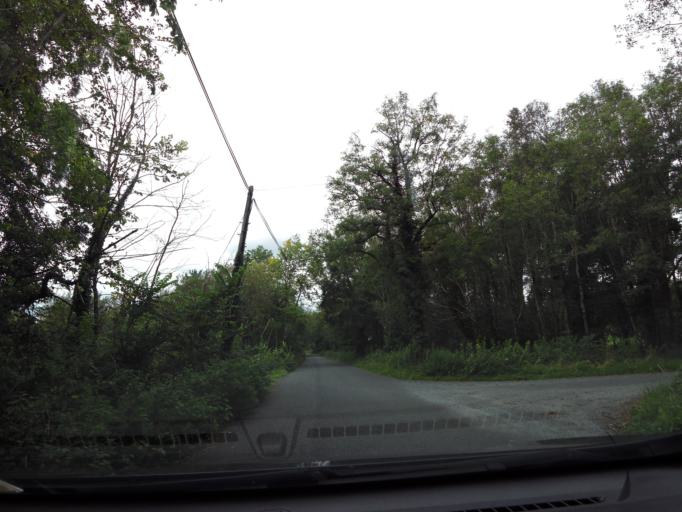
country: IE
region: Connaught
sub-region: County Galway
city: Loughrea
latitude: 53.1549
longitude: -8.4404
